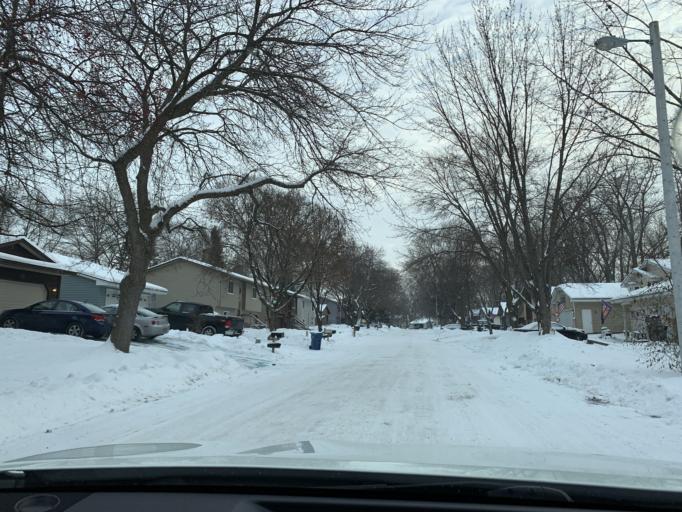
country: US
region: Minnesota
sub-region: Anoka County
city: Coon Rapids
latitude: 45.1590
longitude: -93.2904
